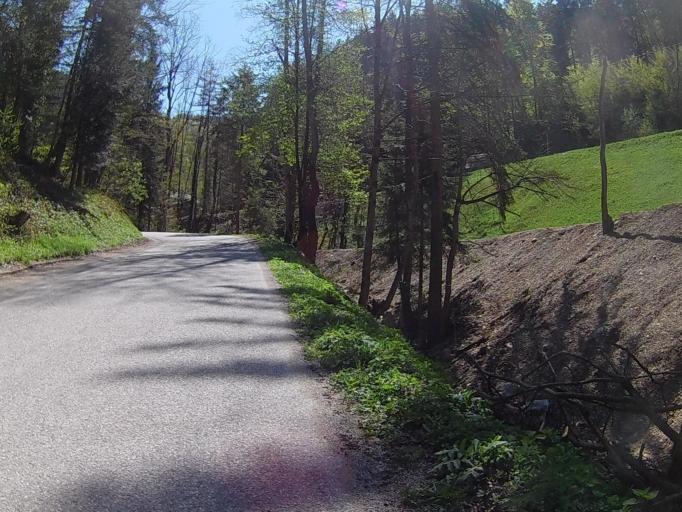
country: SI
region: Ruse
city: Ruse
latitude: 46.5319
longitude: 15.5182
